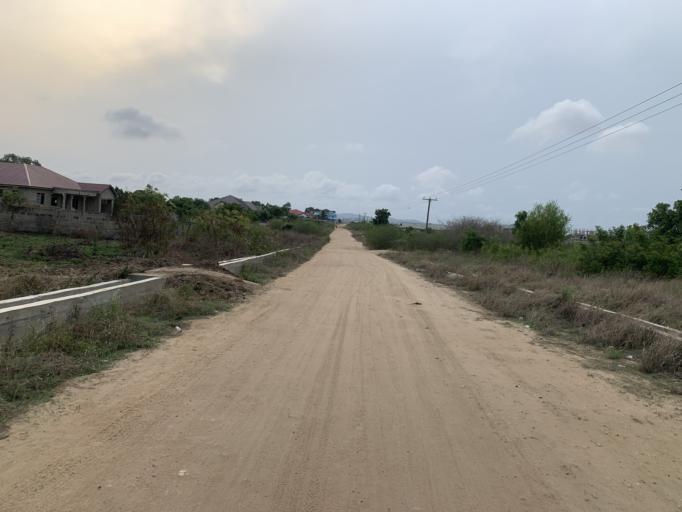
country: GH
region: Central
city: Winneba
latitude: 5.3815
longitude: -0.6225
